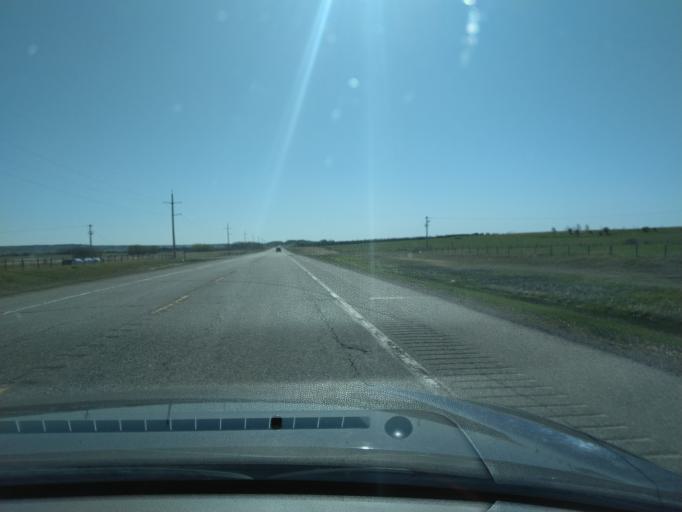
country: CA
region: Alberta
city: Cochrane
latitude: 51.0234
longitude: -114.3754
